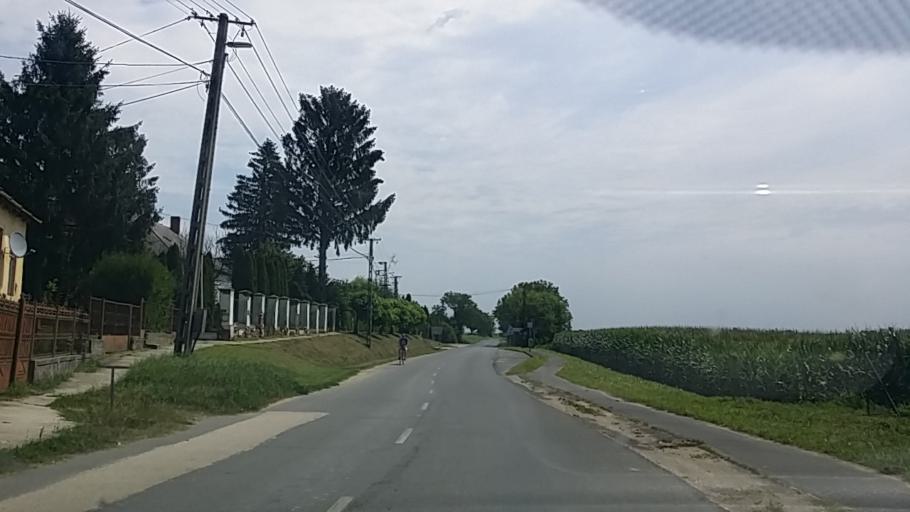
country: HR
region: Medimurska
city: Kotoriba
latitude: 46.3951
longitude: 16.8067
